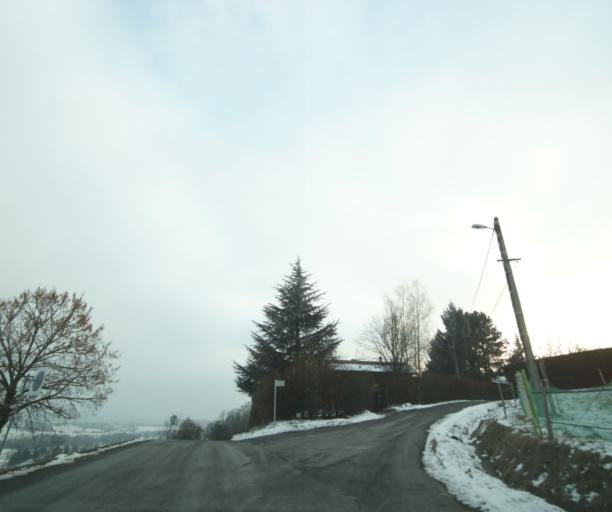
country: FR
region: Rhone-Alpes
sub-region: Departement de la Haute-Savoie
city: Reignier-Esery
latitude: 46.1420
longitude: 6.2382
